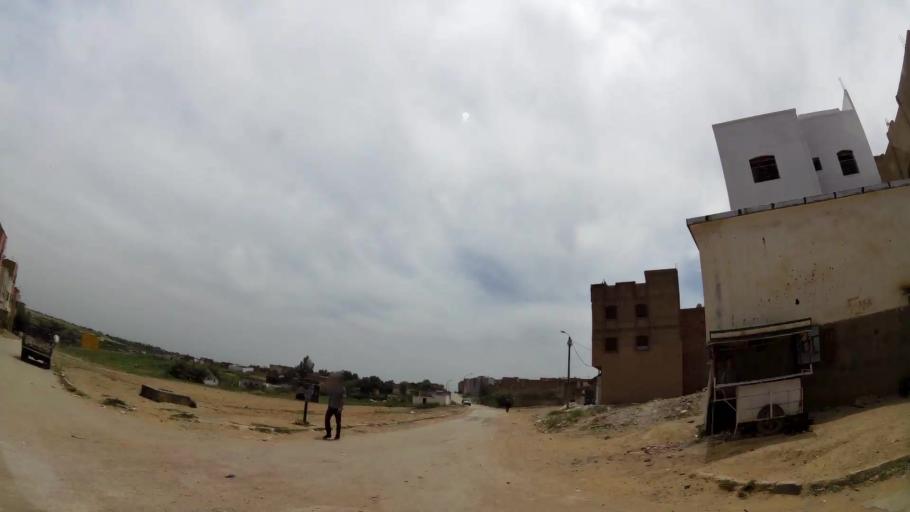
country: MA
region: Rabat-Sale-Zemmour-Zaer
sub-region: Khemisset
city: Khemisset
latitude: 33.8175
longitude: -6.0649
